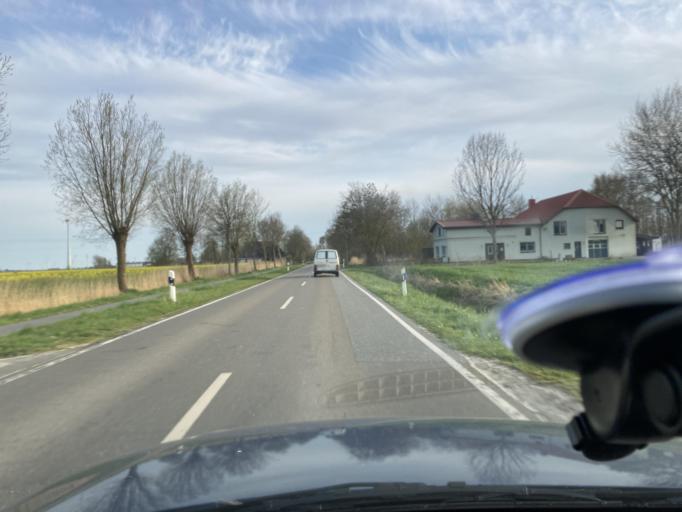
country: DE
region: Schleswig-Holstein
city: Schulp
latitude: 54.2373
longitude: 8.9297
